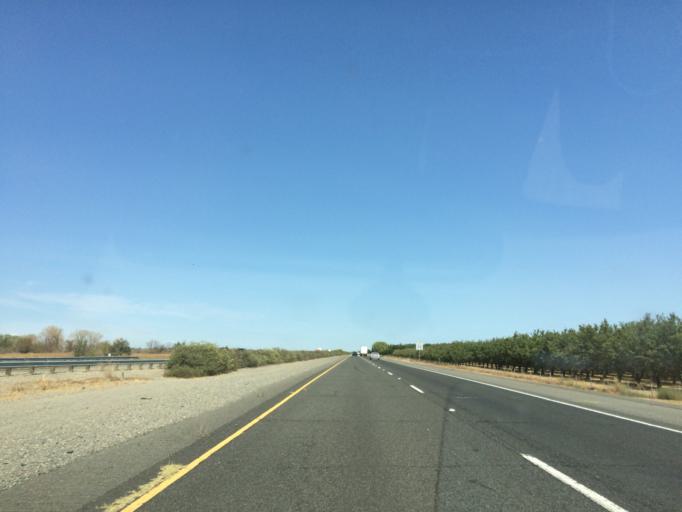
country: US
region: California
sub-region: Glenn County
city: Willows
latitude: 39.6347
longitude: -122.2041
